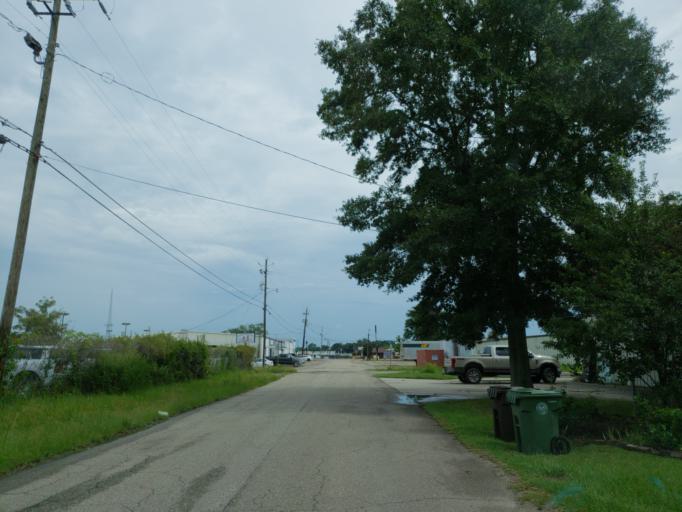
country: US
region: Mississippi
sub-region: Forrest County
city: Hattiesburg
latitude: 31.3159
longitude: -89.3096
